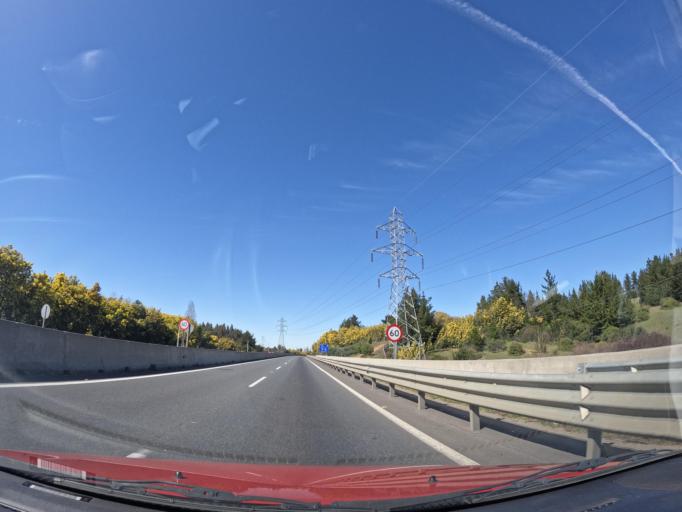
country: CL
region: Biobio
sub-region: Provincia de Biobio
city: Yumbel
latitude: -36.9784
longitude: -72.6348
